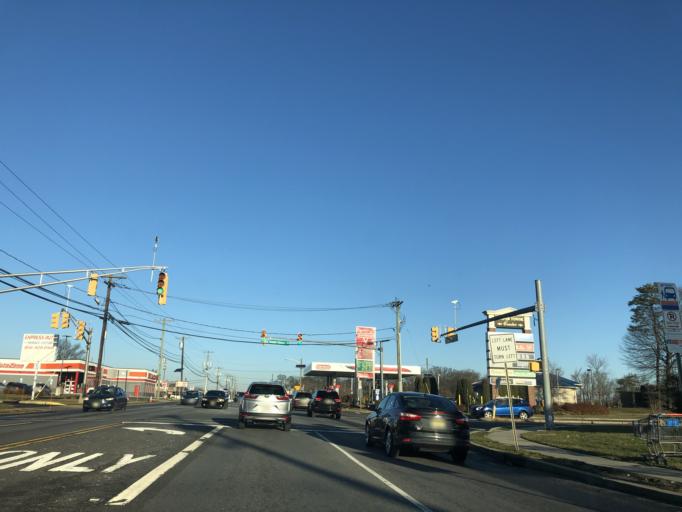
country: US
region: New Jersey
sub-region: Camden County
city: Somerdale
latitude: 39.8532
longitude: -75.0255
